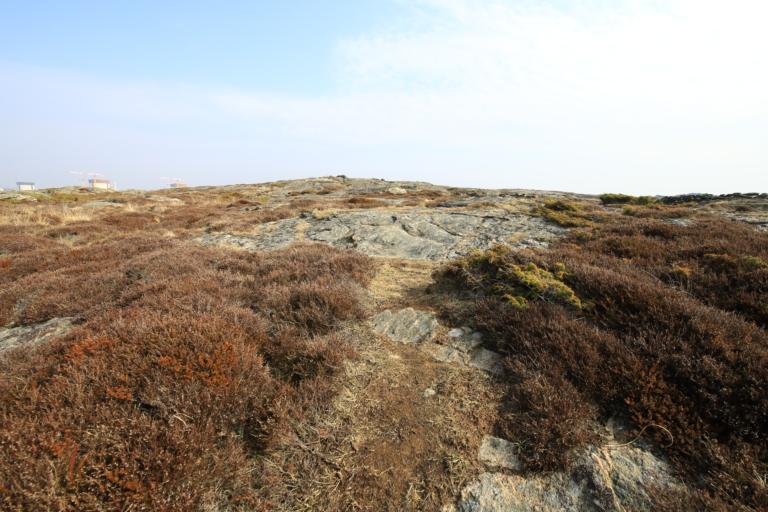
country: SE
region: Halland
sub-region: Kungsbacka Kommun
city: Frillesas
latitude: 57.2546
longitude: 12.0909
